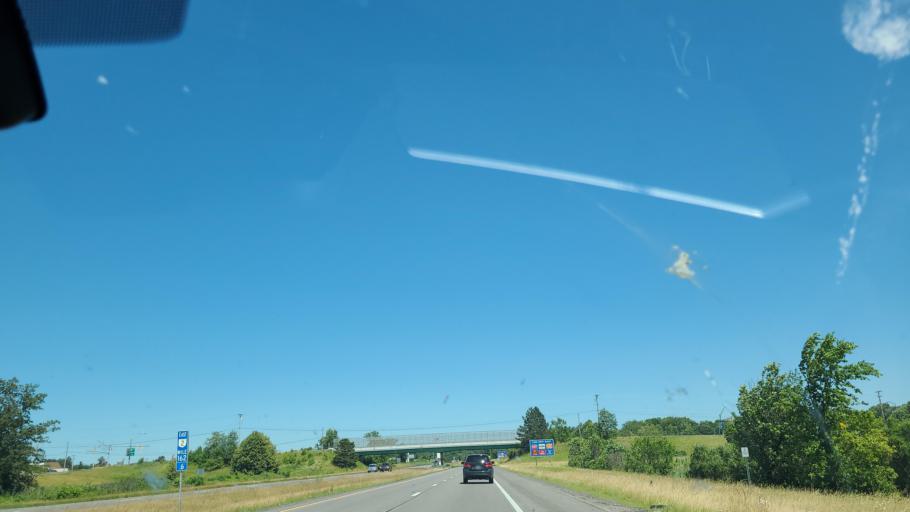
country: US
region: Ohio
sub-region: Lorain County
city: Amherst
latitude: 41.4107
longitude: -82.2418
